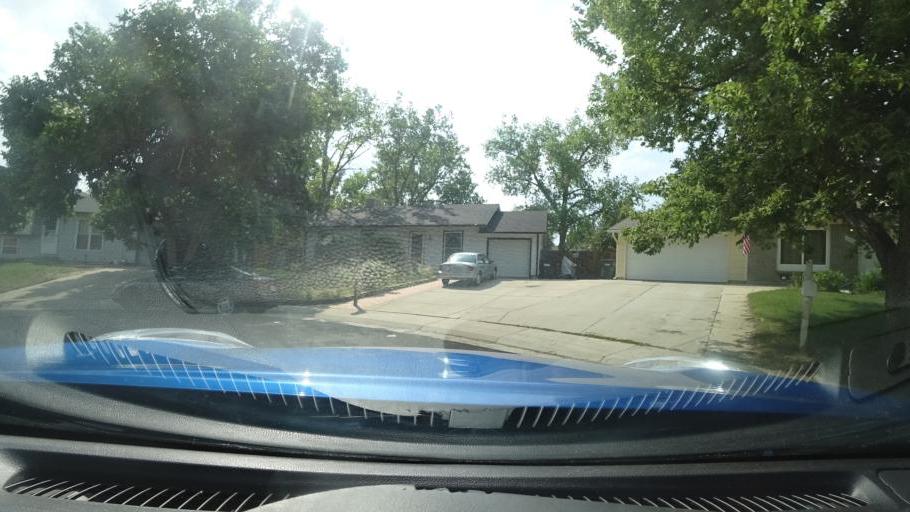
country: US
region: Colorado
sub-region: Adams County
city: Aurora
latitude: 39.6892
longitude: -104.7837
